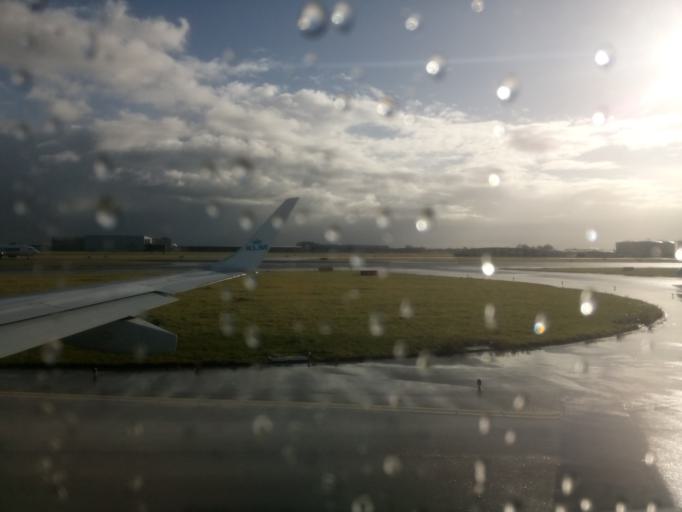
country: NL
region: North Holland
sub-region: Gemeente Aalsmeer
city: Aalsmeer
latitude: 52.3046
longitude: 4.7724
